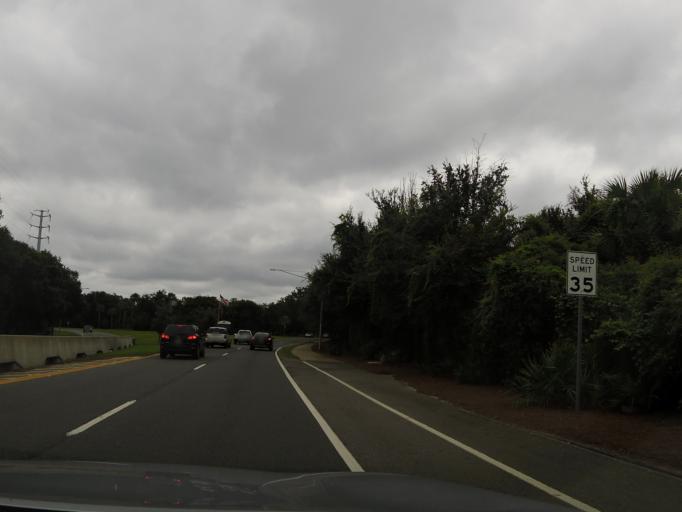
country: US
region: Georgia
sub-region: Glynn County
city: Saint Simon Mills
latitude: 31.1670
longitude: -81.4135
